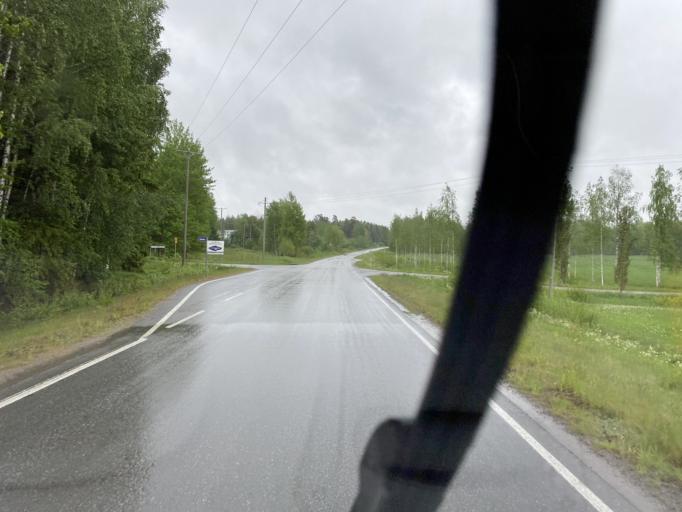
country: FI
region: Pirkanmaa
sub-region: Etelae-Pirkanmaa
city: Urjala
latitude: 61.0424
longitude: 23.4289
